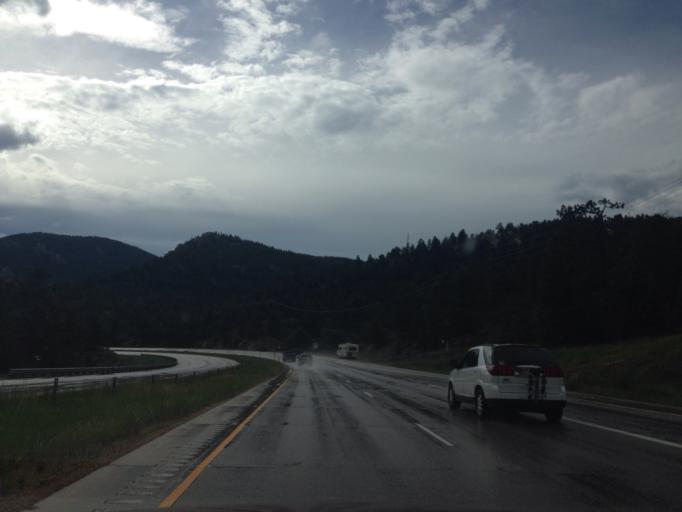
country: US
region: Colorado
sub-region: Jefferson County
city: Indian Hills
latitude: 39.5479
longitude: -105.2612
